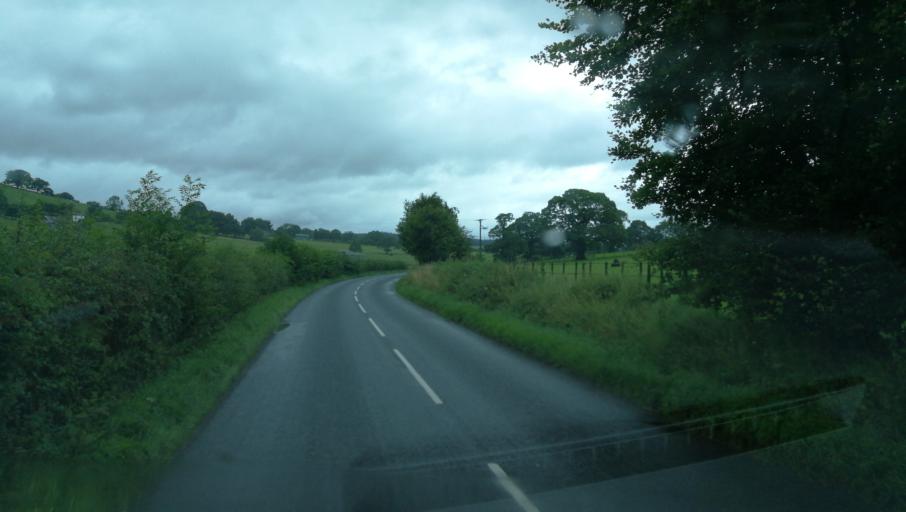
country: GB
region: England
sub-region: Cumbria
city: Penrith
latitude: 54.6147
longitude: -2.8304
